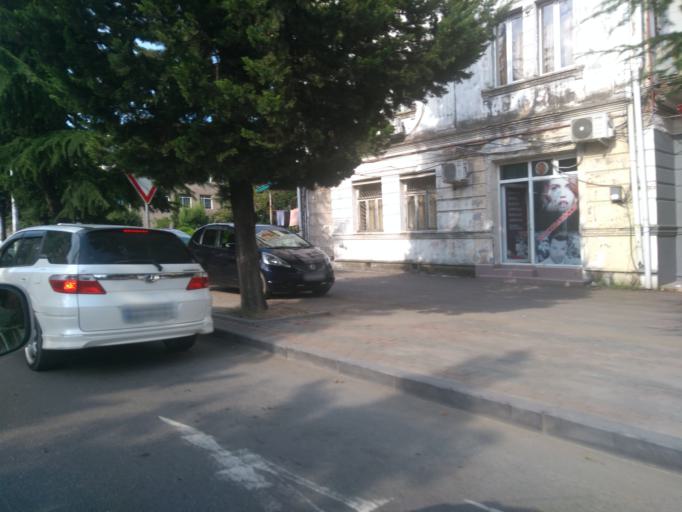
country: GE
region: Ajaria
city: Batumi
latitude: 41.6409
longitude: 41.6248
